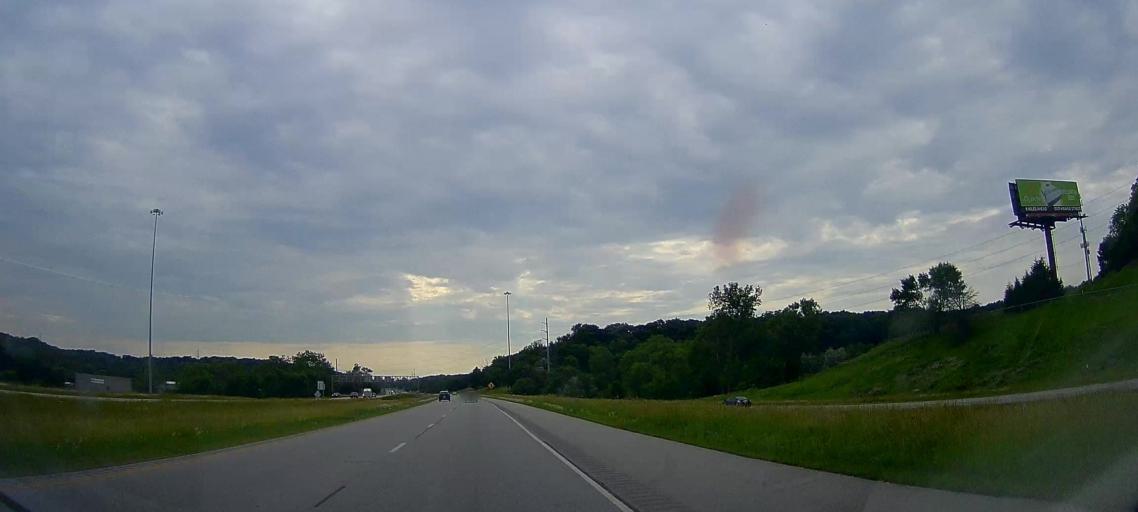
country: US
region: Iowa
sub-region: Pottawattamie County
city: Carter Lake
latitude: 41.3474
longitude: -95.9852
